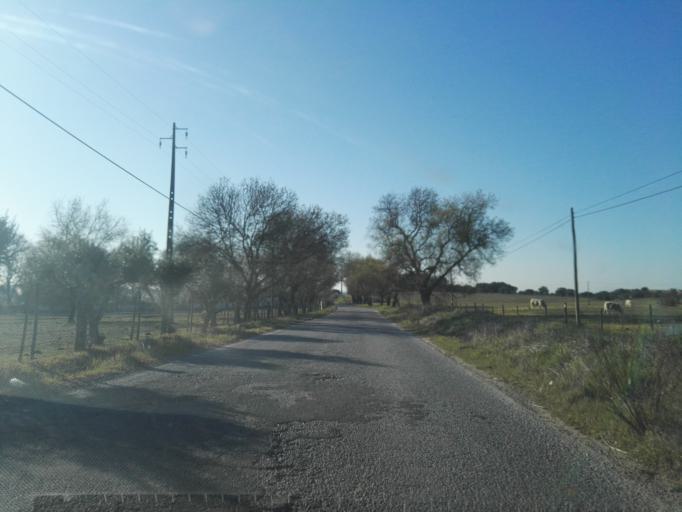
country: PT
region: Evora
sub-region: Evora
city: Evora
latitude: 38.5319
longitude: -7.9500
